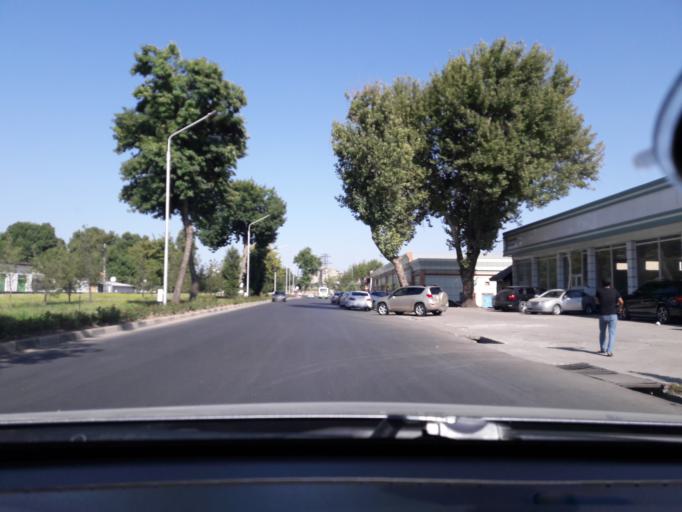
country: TJ
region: Dushanbe
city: Dushanbe
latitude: 38.5692
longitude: 68.7632
